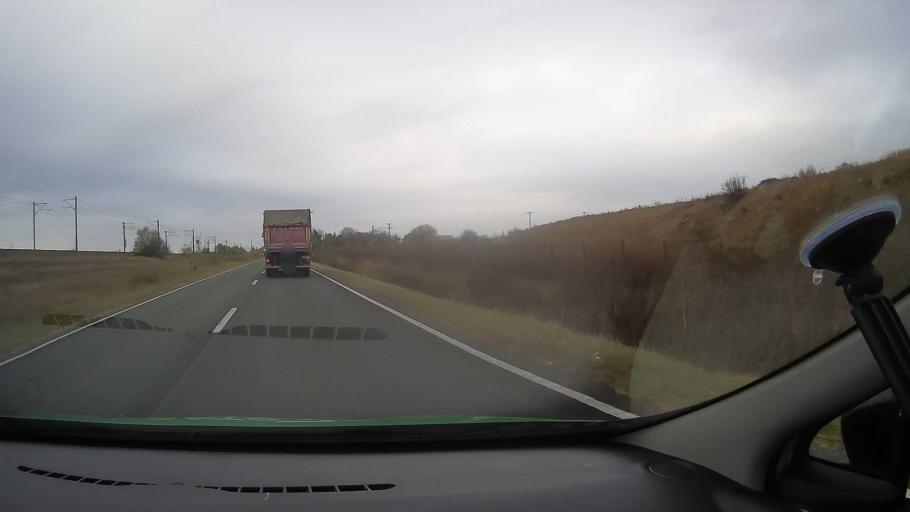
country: RO
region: Constanta
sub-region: Comuna Poarta Alba
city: Poarta Alba
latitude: 44.2252
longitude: 28.3836
